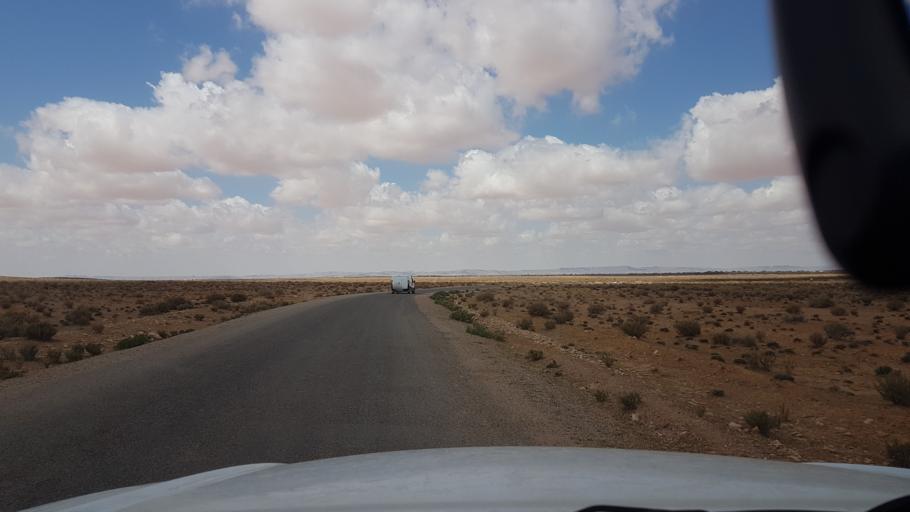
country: TN
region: Madanin
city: Medenine
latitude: 33.2869
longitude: 10.5989
